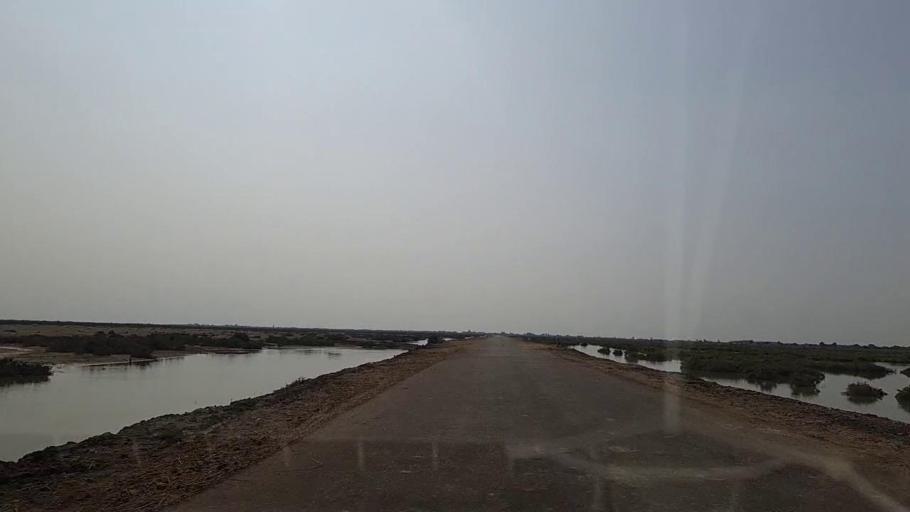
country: PK
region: Sindh
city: Chuhar Jamali
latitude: 24.2119
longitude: 67.8621
